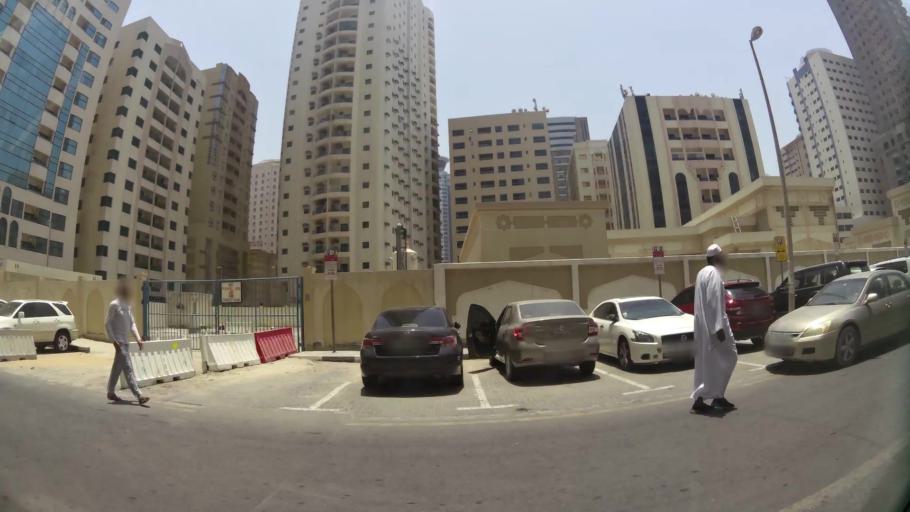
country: AE
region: Ash Shariqah
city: Sharjah
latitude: 25.3270
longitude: 55.3780
